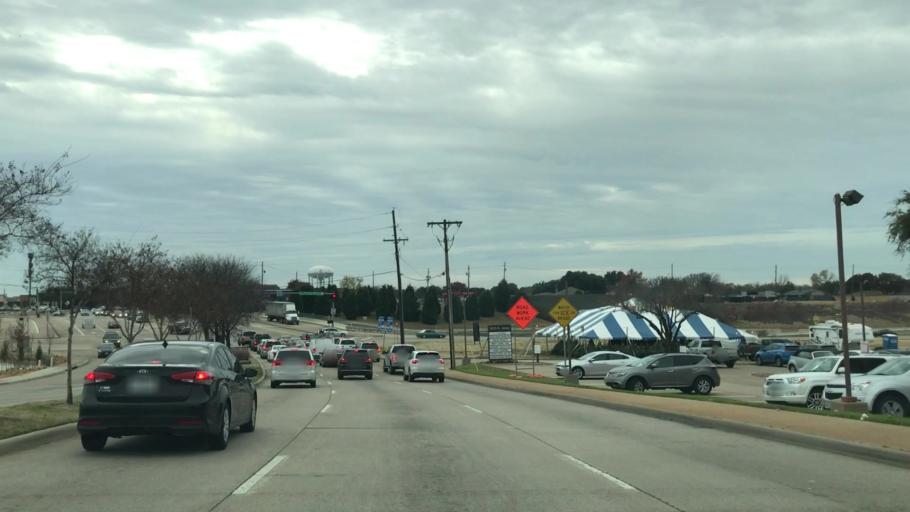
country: US
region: Texas
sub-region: Dallas County
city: Carrollton
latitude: 32.9871
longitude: -96.8909
